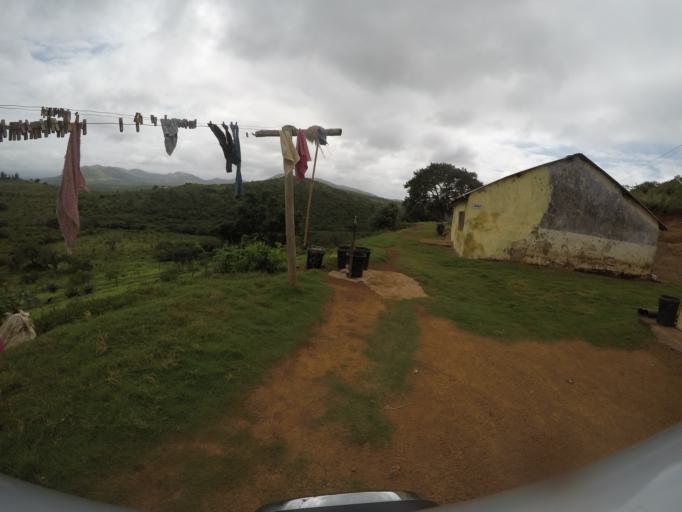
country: ZA
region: KwaZulu-Natal
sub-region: uThungulu District Municipality
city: Empangeni
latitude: -28.6327
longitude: 31.8756
